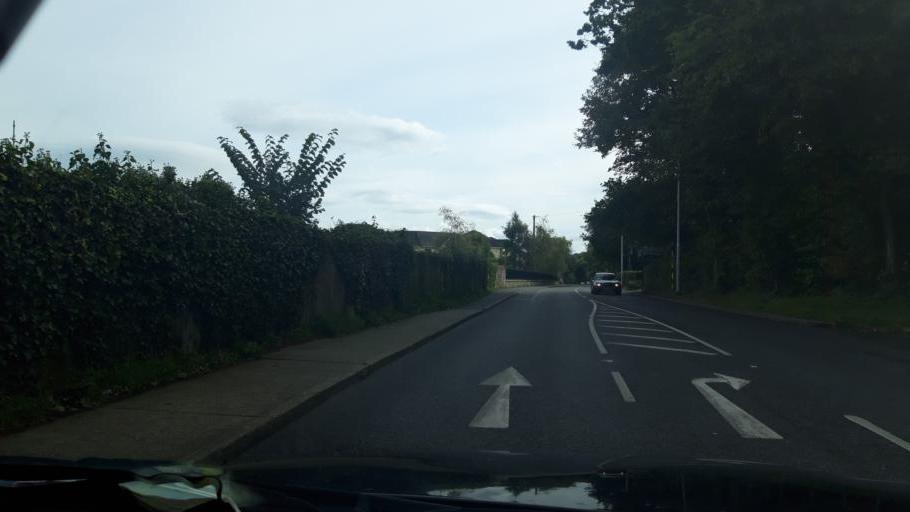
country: IE
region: Leinster
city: Sandyford
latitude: 53.2567
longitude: -6.2207
